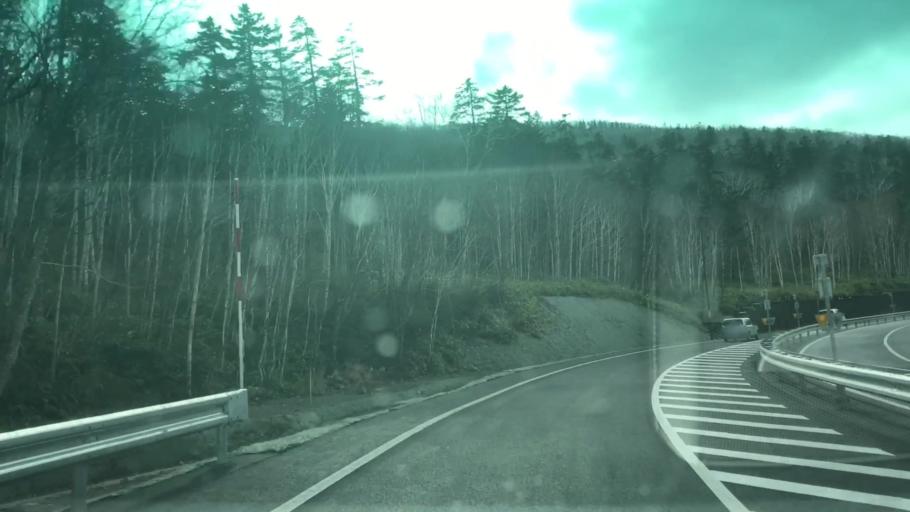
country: JP
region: Hokkaido
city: Otofuke
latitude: 42.9819
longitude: 142.7546
